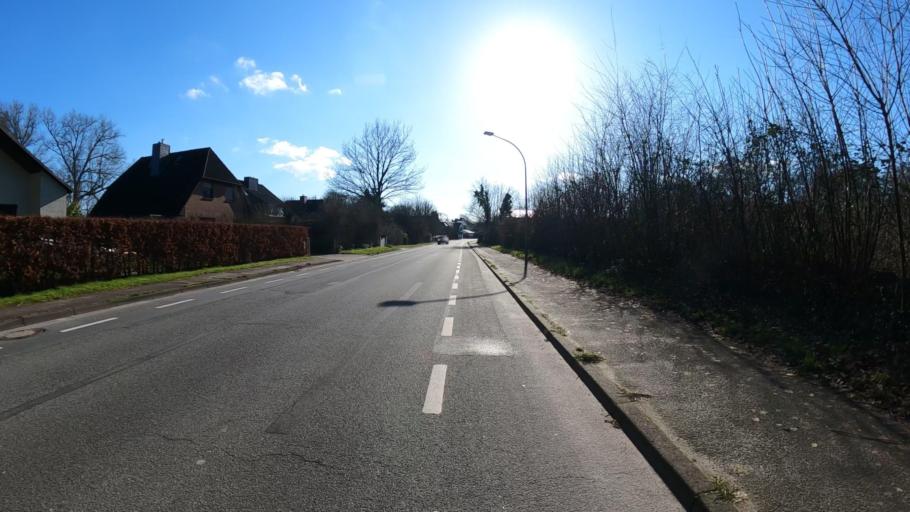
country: DE
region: Schleswig-Holstein
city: Rellingen
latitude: 53.6203
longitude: 9.7982
